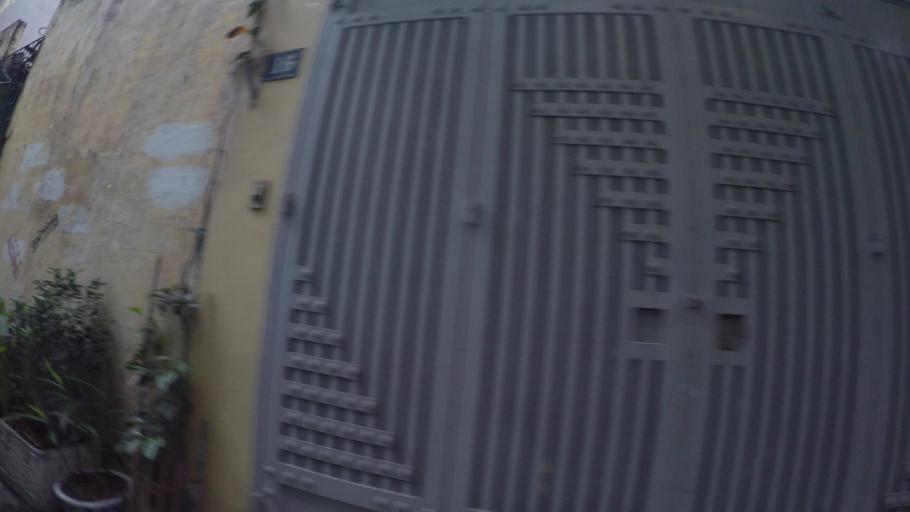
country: VN
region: Ha Noi
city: Hai BaTrung
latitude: 21.0016
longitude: 105.8640
